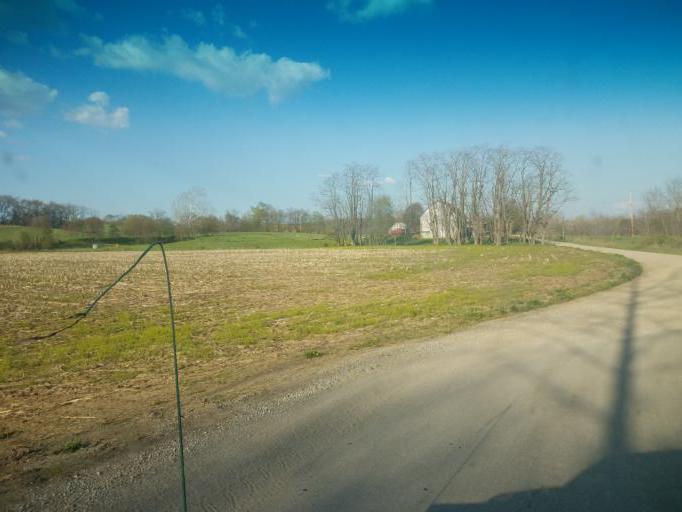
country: US
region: Ohio
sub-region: Wayne County
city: Shreve
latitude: 40.5958
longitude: -82.0465
